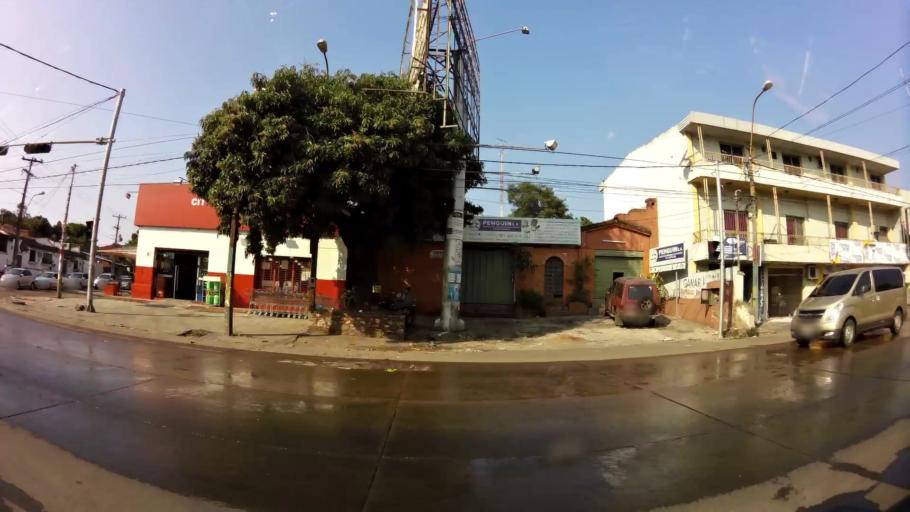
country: PY
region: Central
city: Lambare
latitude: -25.3172
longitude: -57.6075
